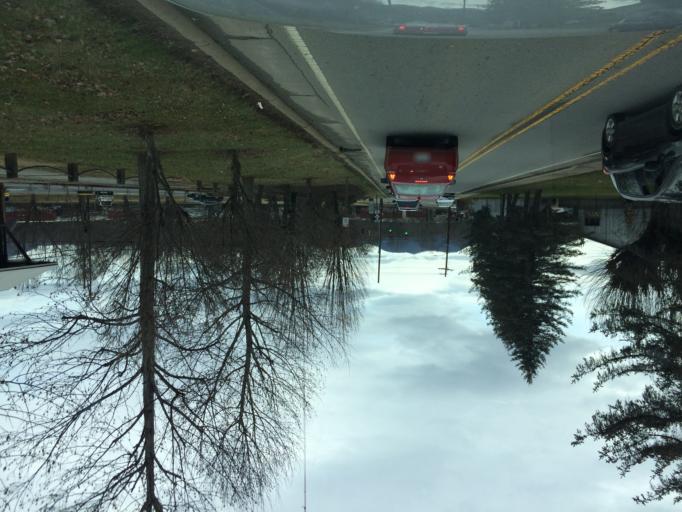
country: US
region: North Carolina
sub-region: Haywood County
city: Canton
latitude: 35.5301
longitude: -82.8440
